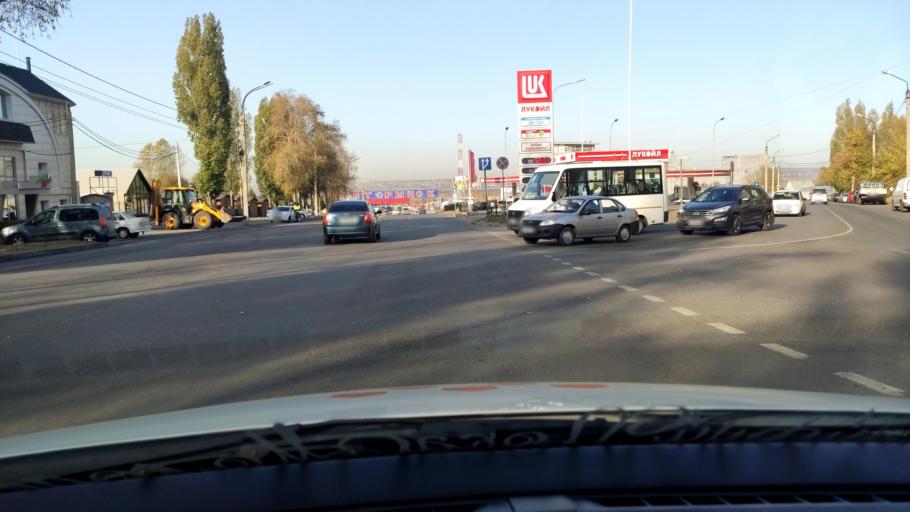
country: RU
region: Voronezj
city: Podgornoye
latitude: 51.7025
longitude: 39.1387
